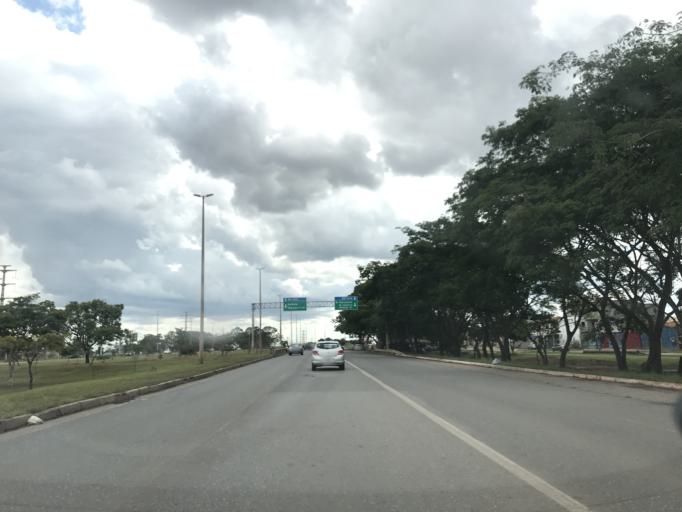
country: BR
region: Federal District
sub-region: Brasilia
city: Brasilia
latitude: -15.8787
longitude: -48.0528
